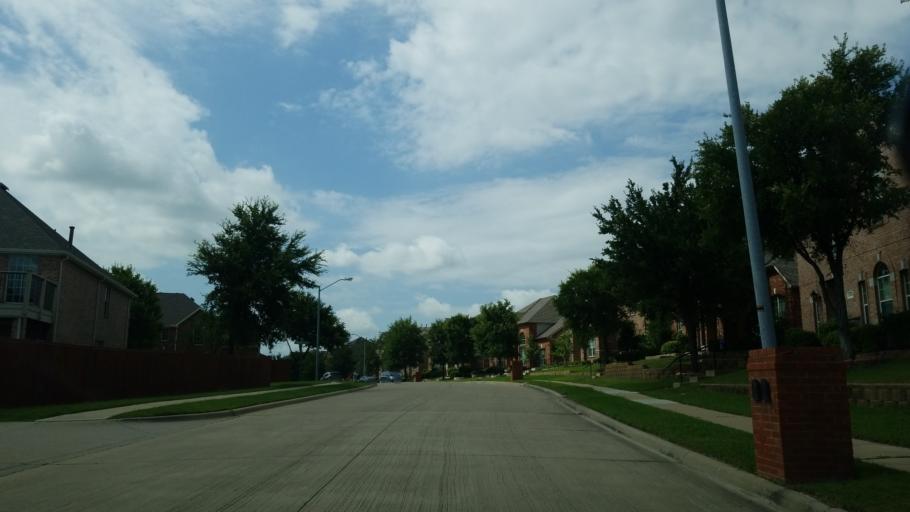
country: US
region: Texas
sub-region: Dallas County
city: Coppell
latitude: 32.9305
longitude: -96.9632
